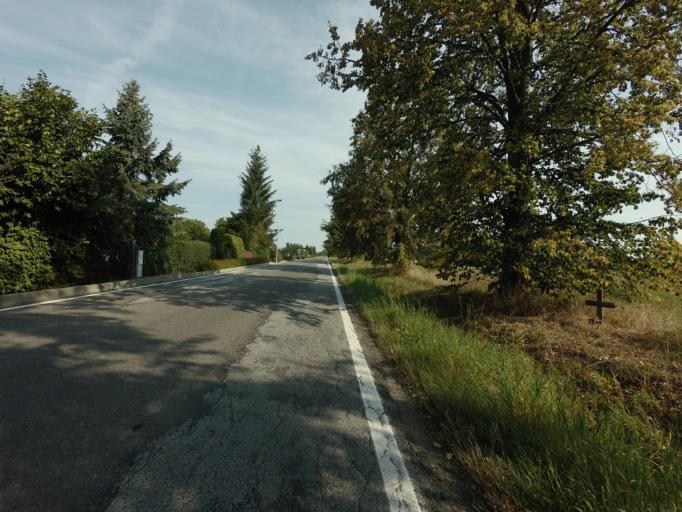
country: CZ
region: Jihocesky
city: Milevsko
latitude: 49.4614
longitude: 14.3631
